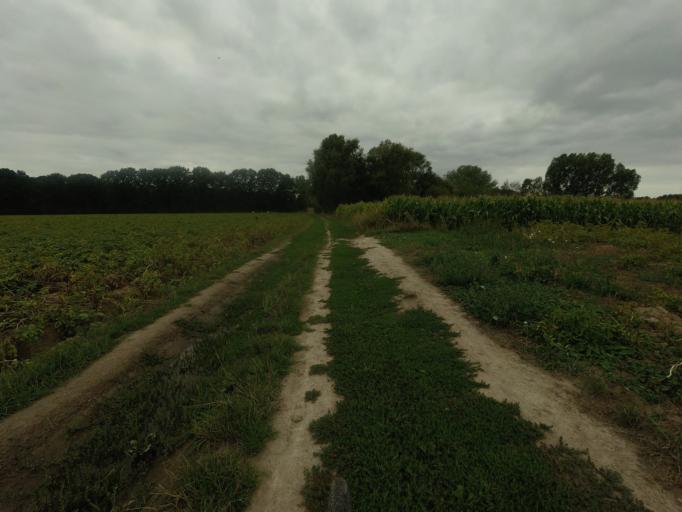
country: BE
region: Flanders
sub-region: Provincie Vlaams-Brabant
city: Herent
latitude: 50.9183
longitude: 4.6229
